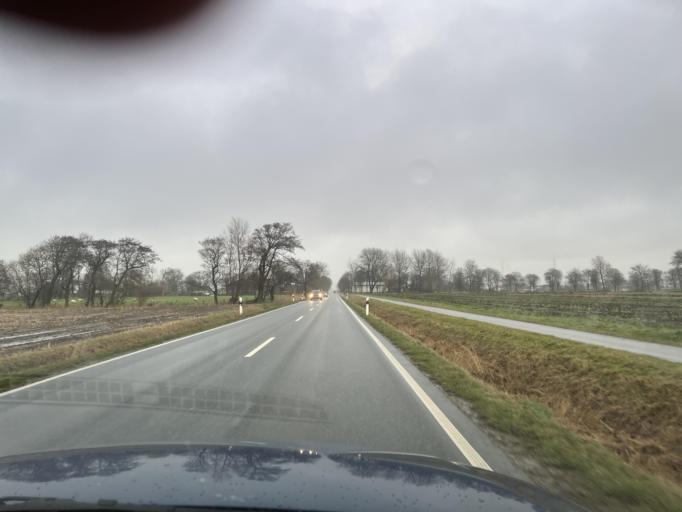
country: DE
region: Schleswig-Holstein
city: Oesterwurth
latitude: 54.2123
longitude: 8.9811
